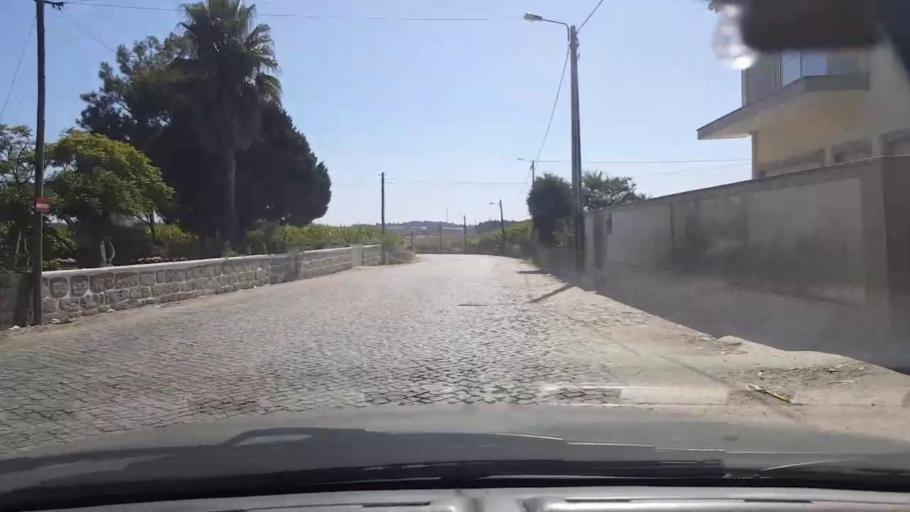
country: PT
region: Porto
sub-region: Matosinhos
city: Lavra
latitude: 41.2767
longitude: -8.7173
